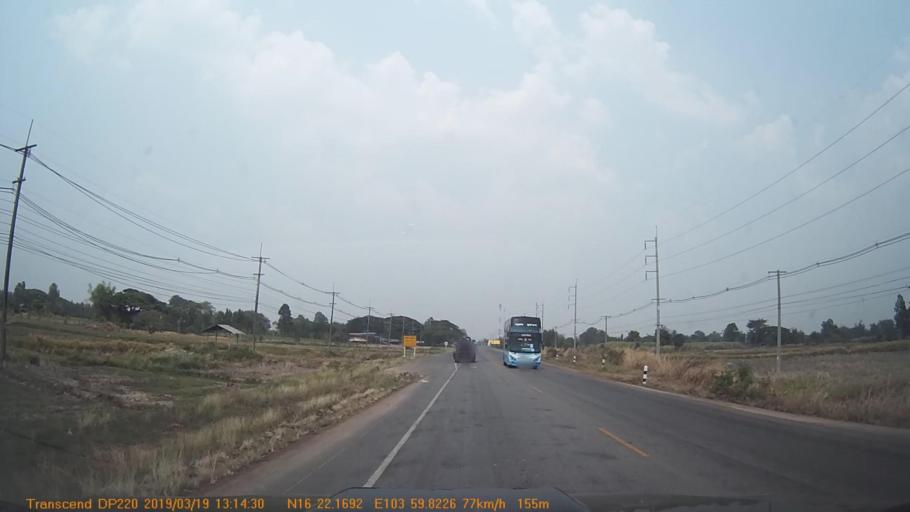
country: TH
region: Roi Et
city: Waeng
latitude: 16.3696
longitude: 103.9971
